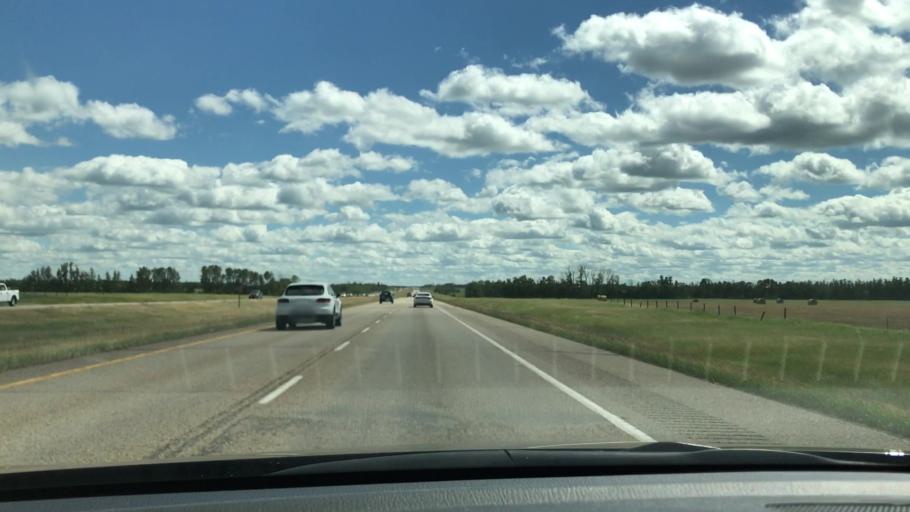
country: CA
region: Alberta
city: Leduc
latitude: 53.1530
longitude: -113.5984
